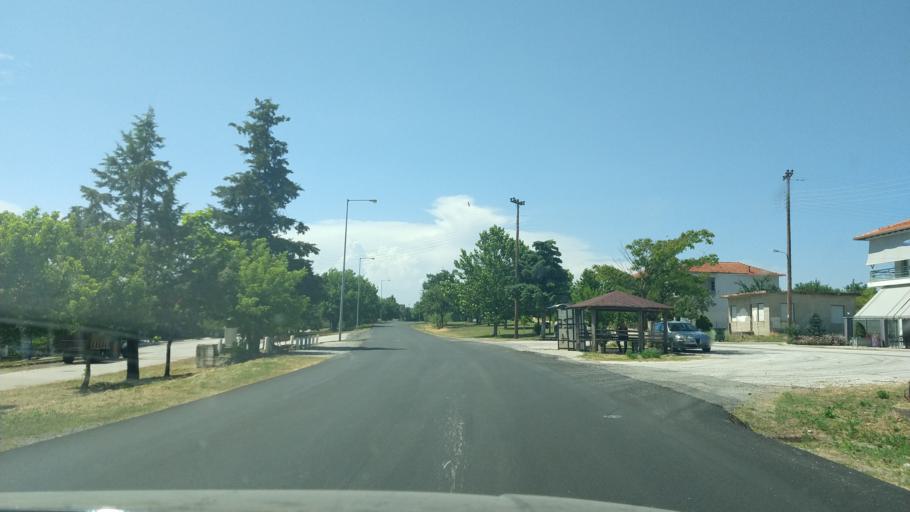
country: GR
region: West Macedonia
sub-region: Nomos Grevenon
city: Grevena
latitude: 39.9832
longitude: 21.5042
